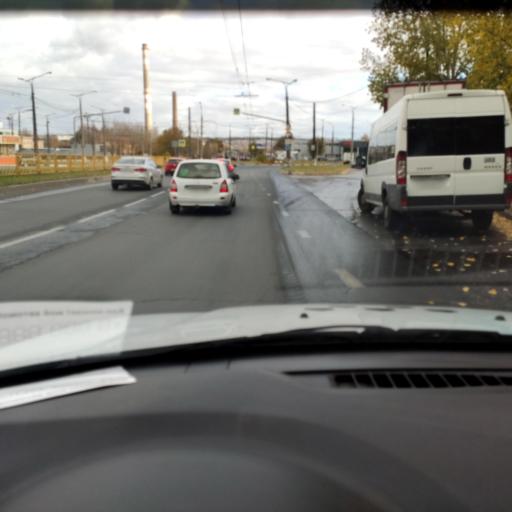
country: RU
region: Samara
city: Zhigulevsk
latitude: 53.4865
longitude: 49.4844
